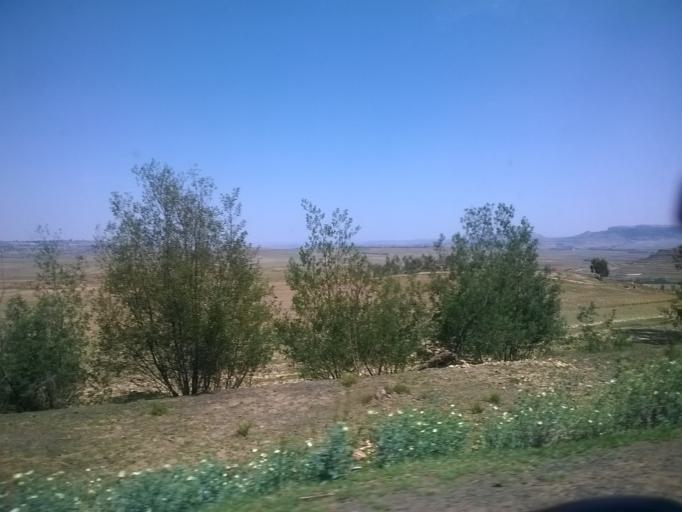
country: LS
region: Berea
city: Teyateyaneng
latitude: -29.1148
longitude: 27.7983
